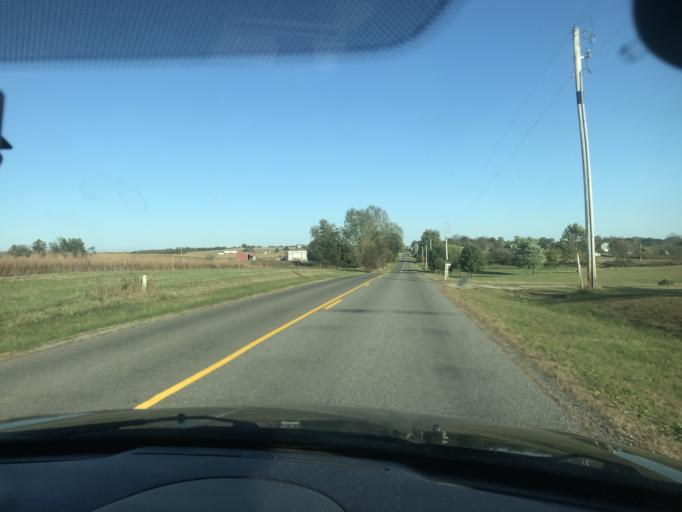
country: US
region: Ohio
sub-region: Logan County
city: De Graff
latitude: 40.3223
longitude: -83.8424
